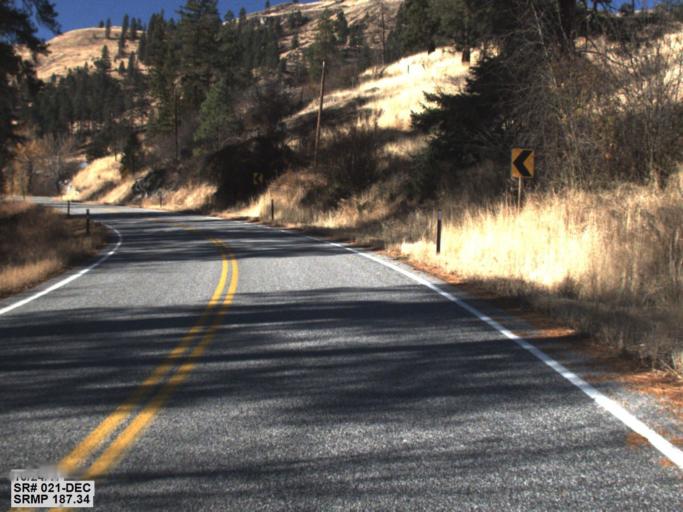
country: CA
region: British Columbia
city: Grand Forks
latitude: 48.9559
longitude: -118.5402
